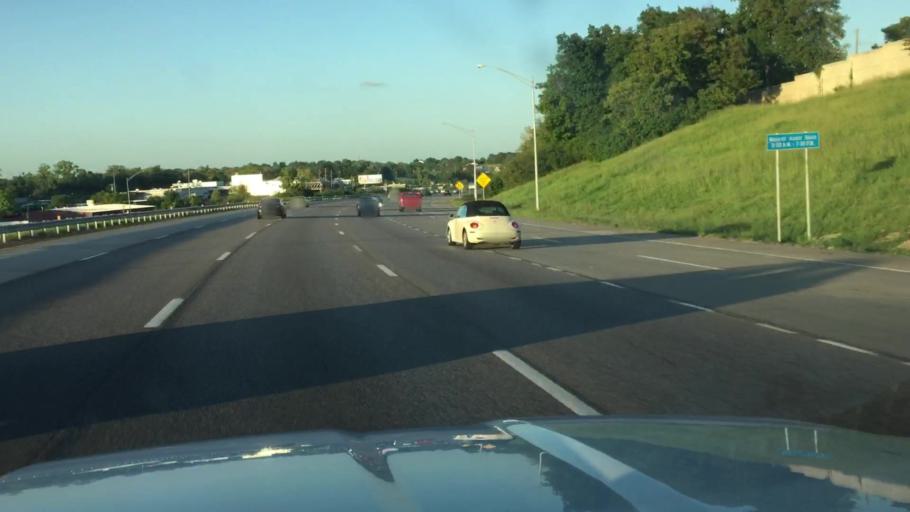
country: US
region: Missouri
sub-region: Saint Louis County
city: Green Park
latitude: 38.5181
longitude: -90.3320
